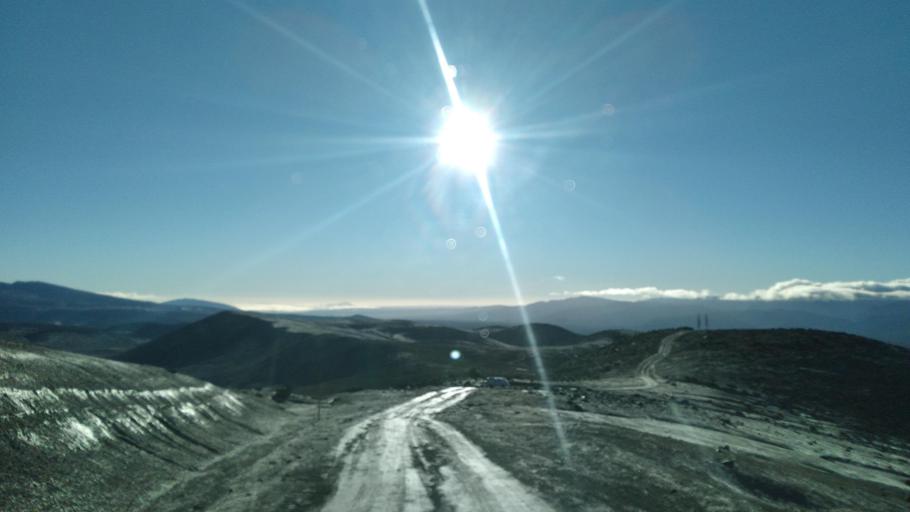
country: NZ
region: Manawatu-Wanganui
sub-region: Ruapehu District
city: Waiouru
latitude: -39.2695
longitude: 175.6496
